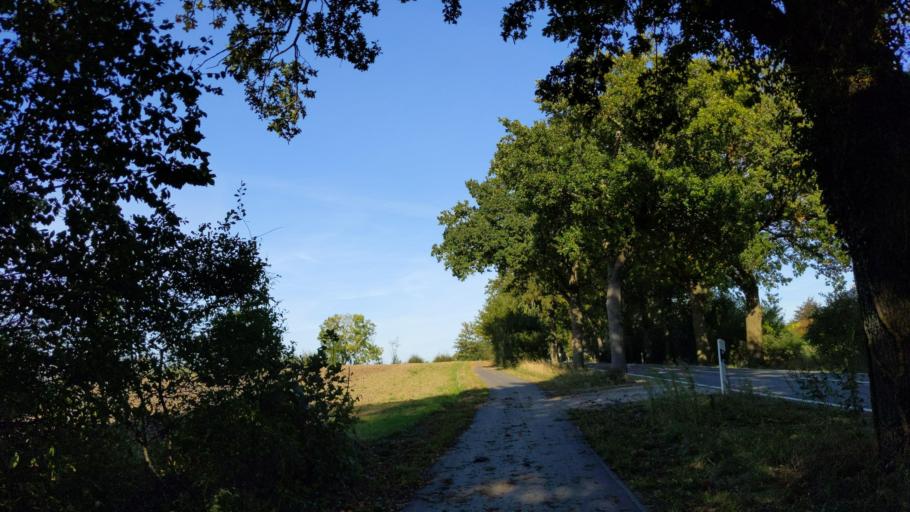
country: DE
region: Schleswig-Holstein
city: Eutin
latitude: 54.1144
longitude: 10.5920
